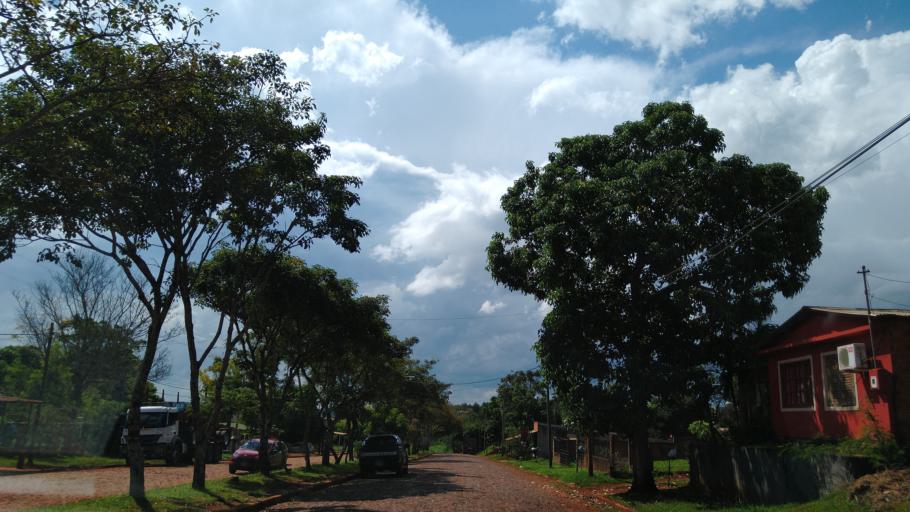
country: AR
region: Misiones
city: Puerto Libertad
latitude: -25.9631
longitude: -54.5603
